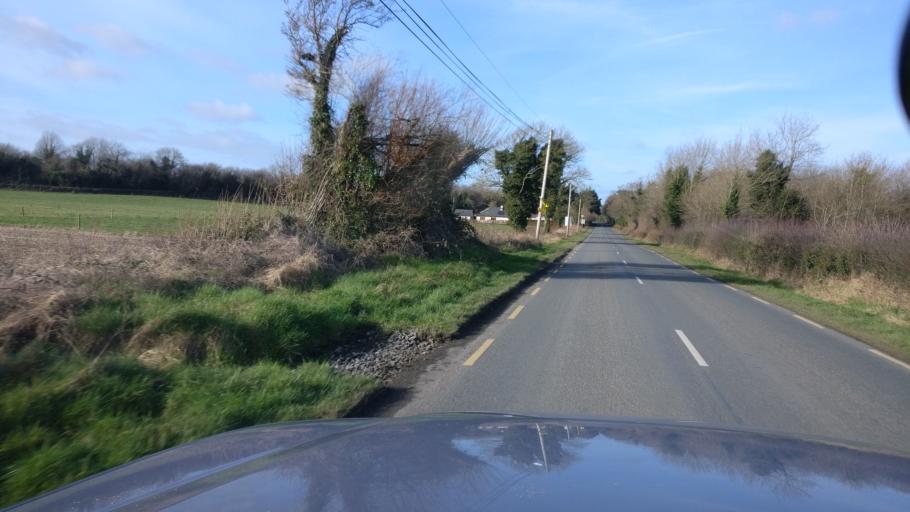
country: IE
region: Leinster
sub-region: Laois
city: Stradbally
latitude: 52.9646
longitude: -7.2046
